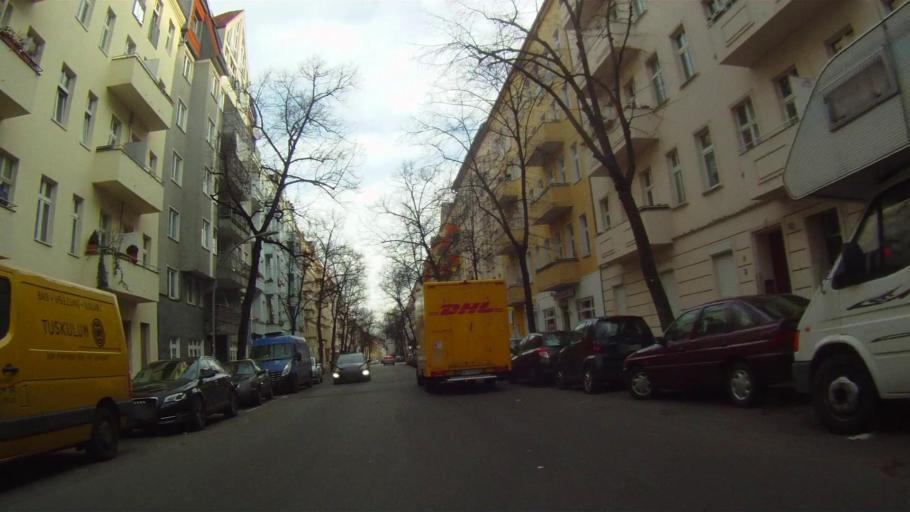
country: DE
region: Berlin
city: Britz
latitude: 52.4689
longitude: 13.4343
